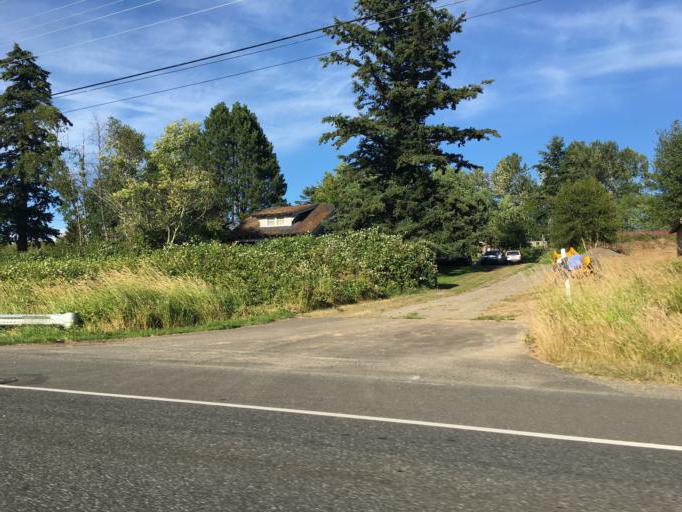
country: US
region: Washington
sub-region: Whatcom County
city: Bellingham
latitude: 48.8260
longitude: -122.4859
